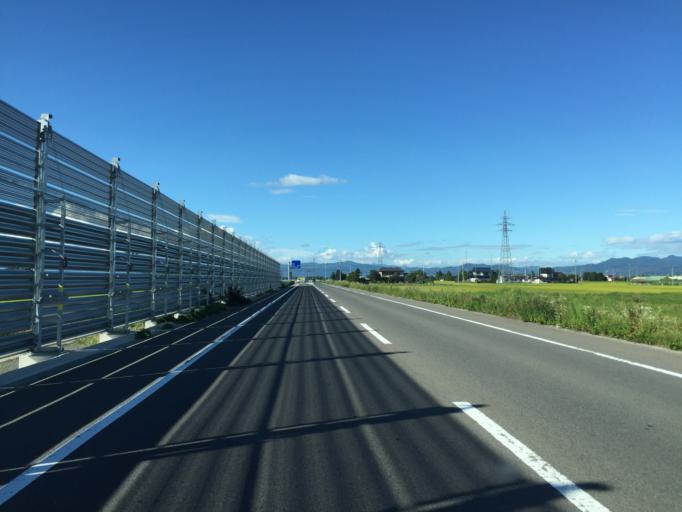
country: JP
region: Yamagata
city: Yonezawa
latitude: 37.9526
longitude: 140.1124
